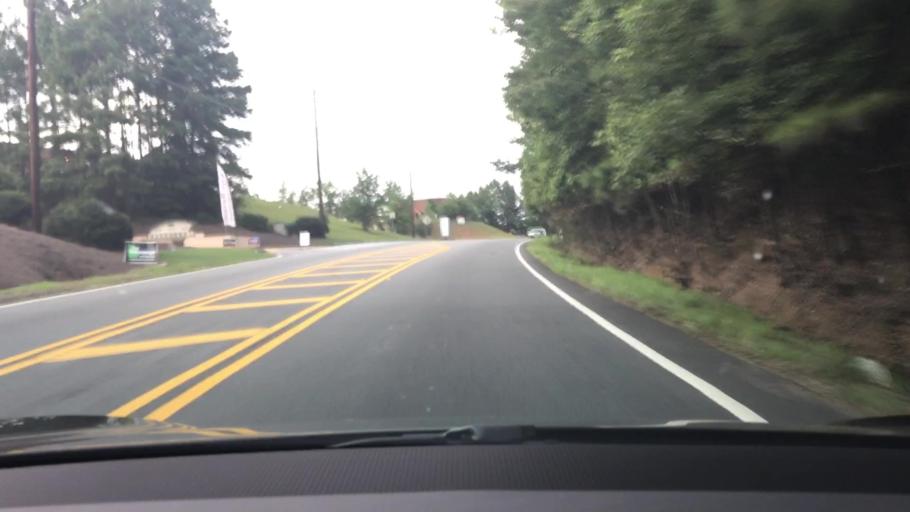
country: US
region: Georgia
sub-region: Gwinnett County
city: Suwanee
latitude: 34.0343
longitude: -84.0883
